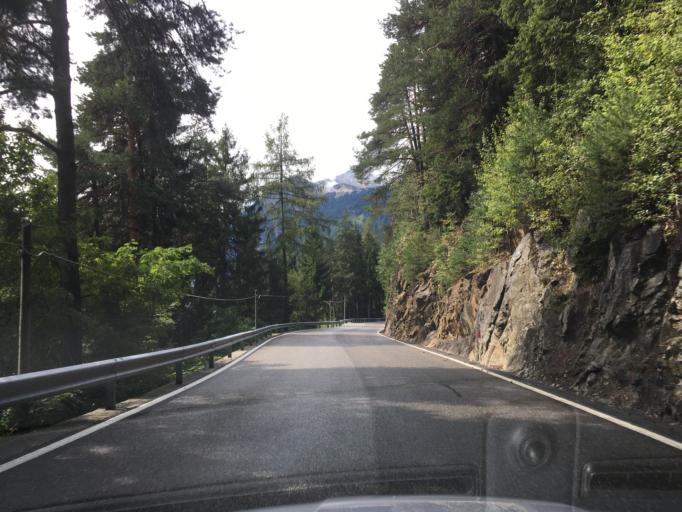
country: IT
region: Trentino-Alto Adige
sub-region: Bolzano
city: San Leonardo in Passiria
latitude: 46.8213
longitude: 11.2571
